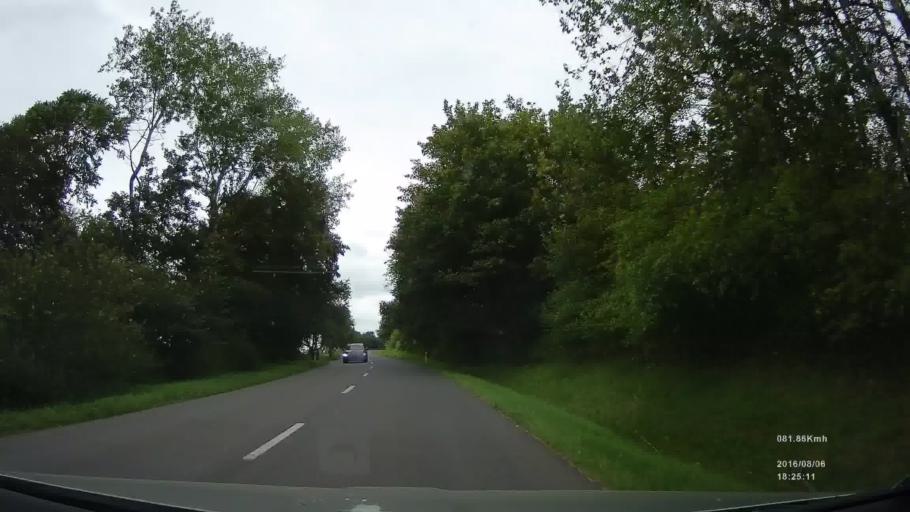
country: SK
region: Presovsky
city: Svidnik
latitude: 49.2926
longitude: 21.5731
